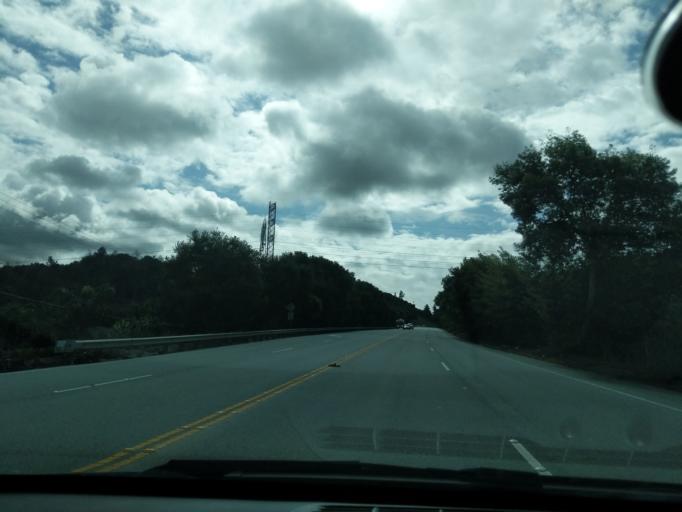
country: US
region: California
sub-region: San Benito County
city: Aromas
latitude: 36.8879
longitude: -121.6664
